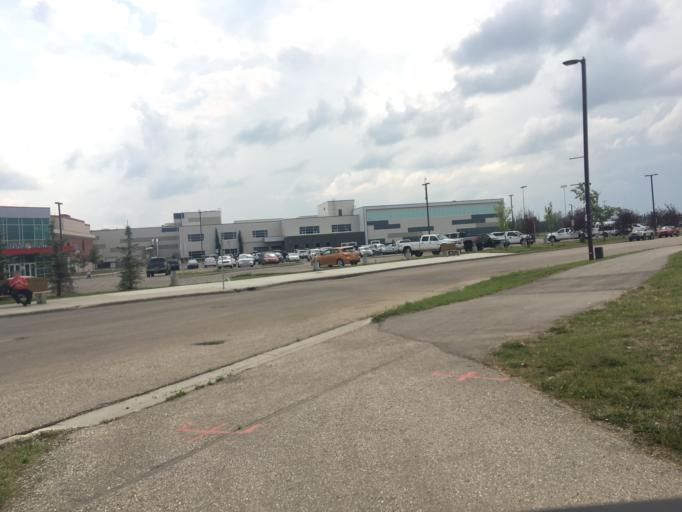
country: CA
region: Alberta
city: Grande Prairie
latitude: 55.1450
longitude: -118.8144
